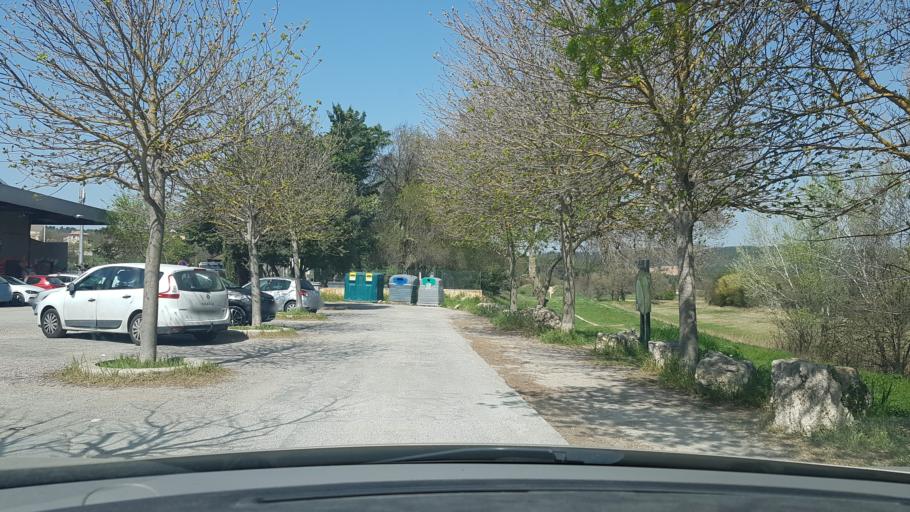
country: FR
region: Provence-Alpes-Cote d'Azur
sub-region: Departement des Bouches-du-Rhone
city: Gardanne
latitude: 43.4593
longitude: 5.4623
